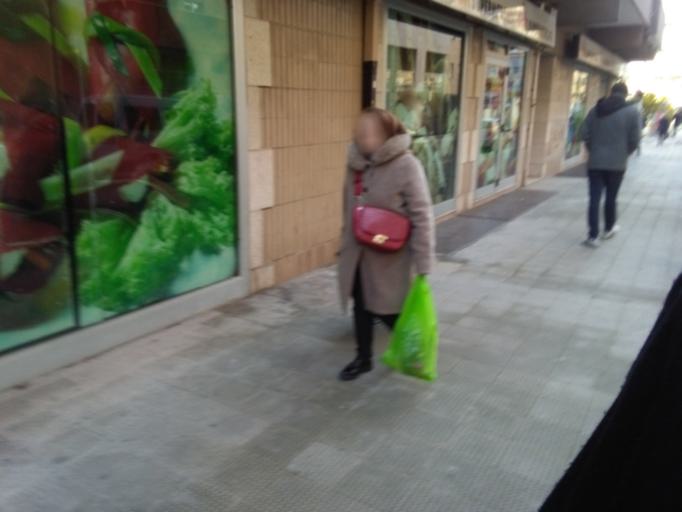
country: IT
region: Apulia
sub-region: Provincia di Barletta - Andria - Trani
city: Andria
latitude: 41.2308
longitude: 16.2994
